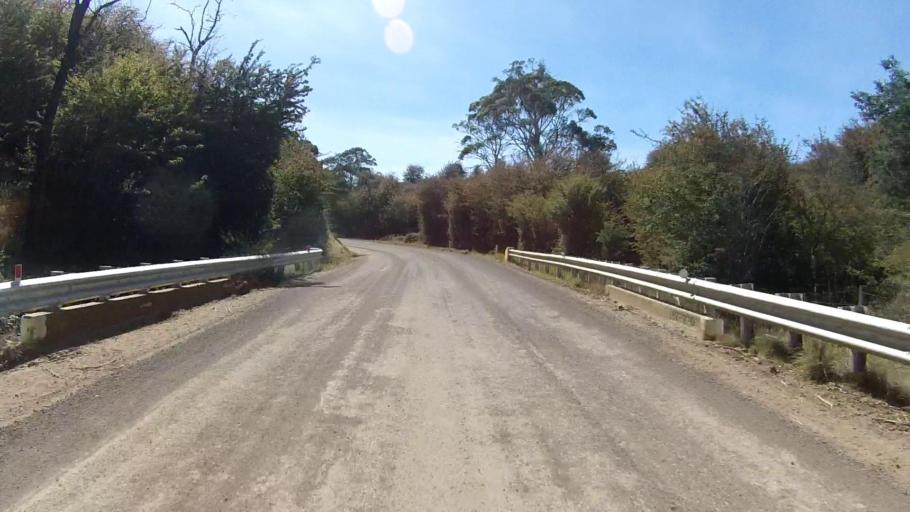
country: AU
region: Tasmania
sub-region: Sorell
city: Sorell
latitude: -42.7582
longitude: 147.6580
